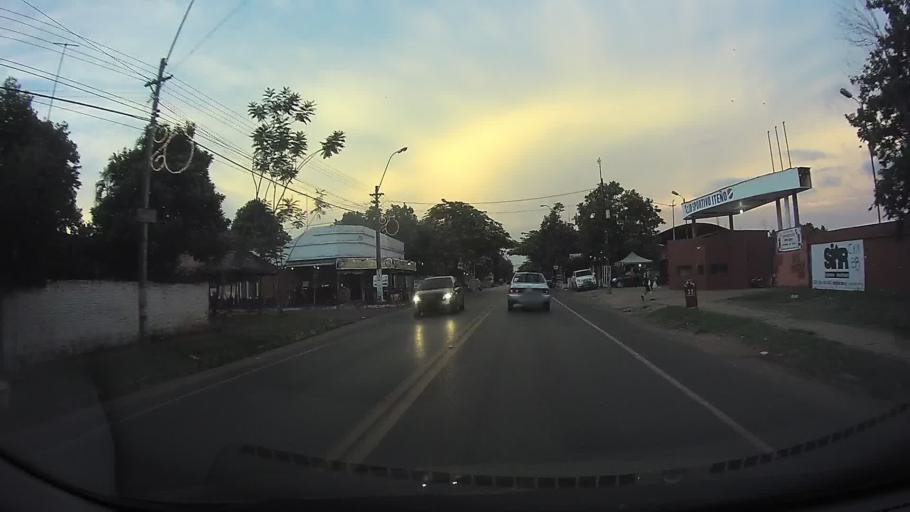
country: PY
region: Central
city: Ita
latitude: -25.5093
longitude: -57.3568
